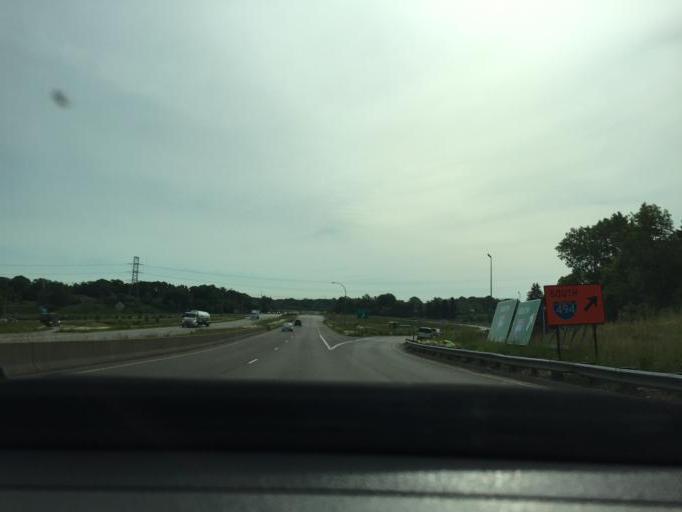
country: US
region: Minnesota
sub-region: Hennepin County
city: Hopkins
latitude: 44.9239
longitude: -93.4558
